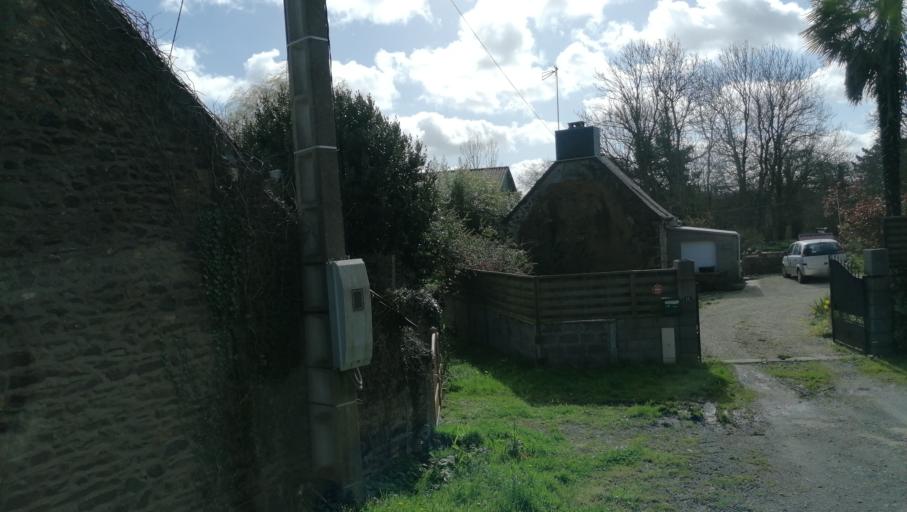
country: FR
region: Brittany
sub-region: Departement des Cotes-d'Armor
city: Pleguien
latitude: 48.6343
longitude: -2.9210
